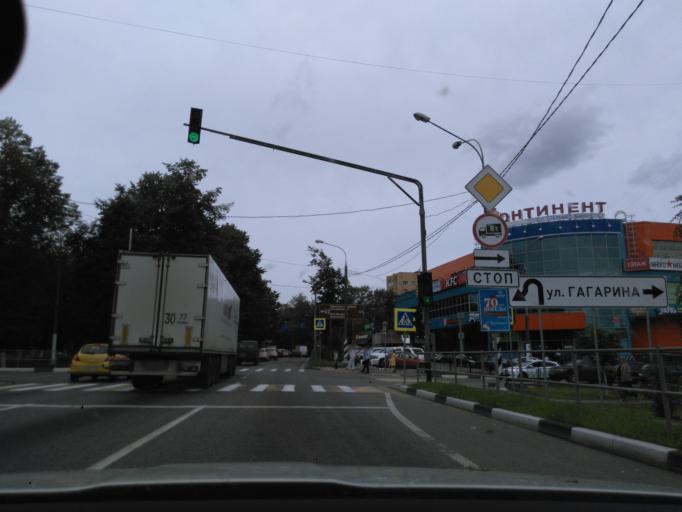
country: RU
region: Moskovskaya
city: Klin
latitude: 56.3315
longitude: 36.7296
